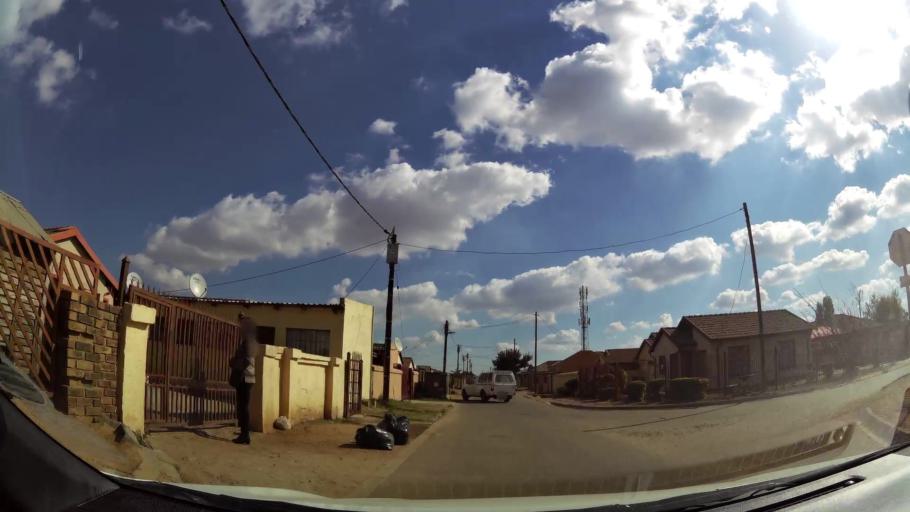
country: ZA
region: Gauteng
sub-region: City of Tshwane Metropolitan Municipality
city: Cullinan
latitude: -25.7063
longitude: 28.4115
